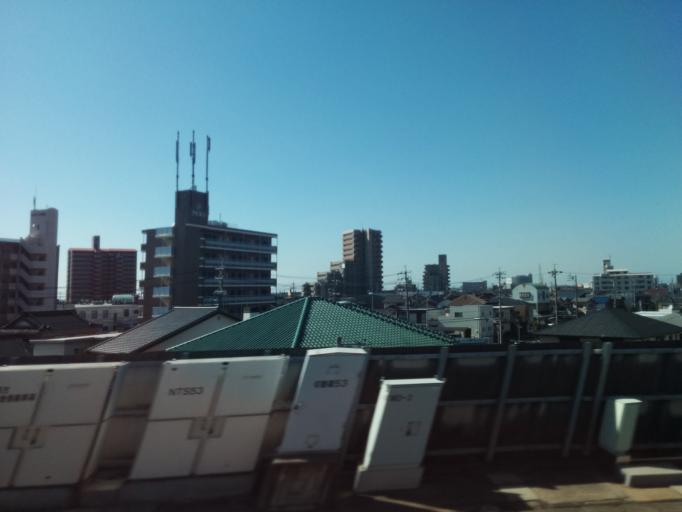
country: JP
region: Aichi
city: Anjo
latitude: 34.9711
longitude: 137.0585
